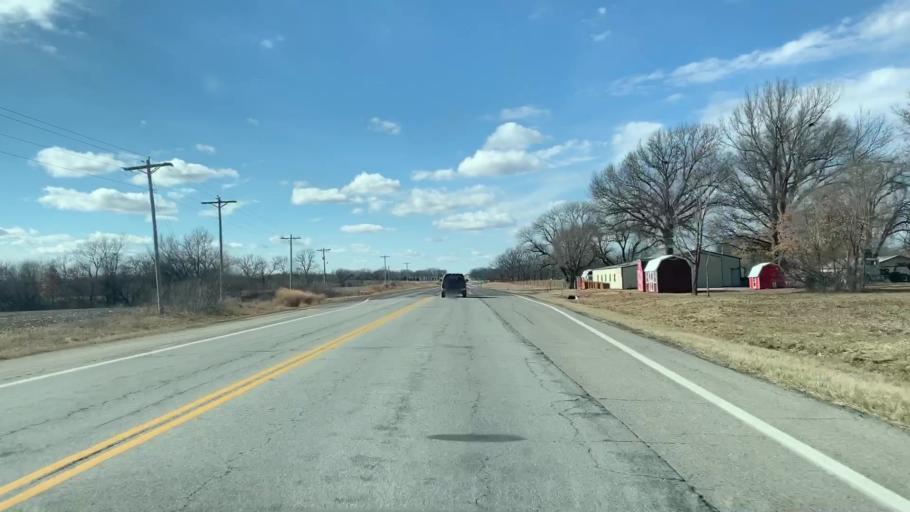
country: US
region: Kansas
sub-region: Labette County
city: Parsons
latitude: 37.3404
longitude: -95.1294
